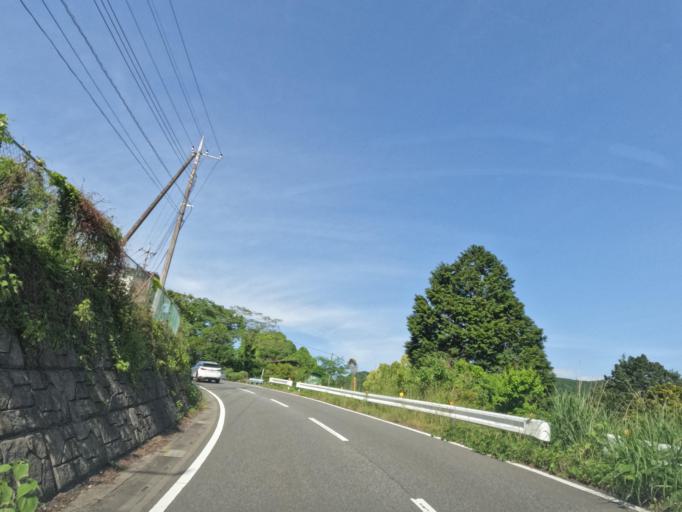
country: JP
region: Saitama
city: Yorii
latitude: 36.0466
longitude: 139.1706
